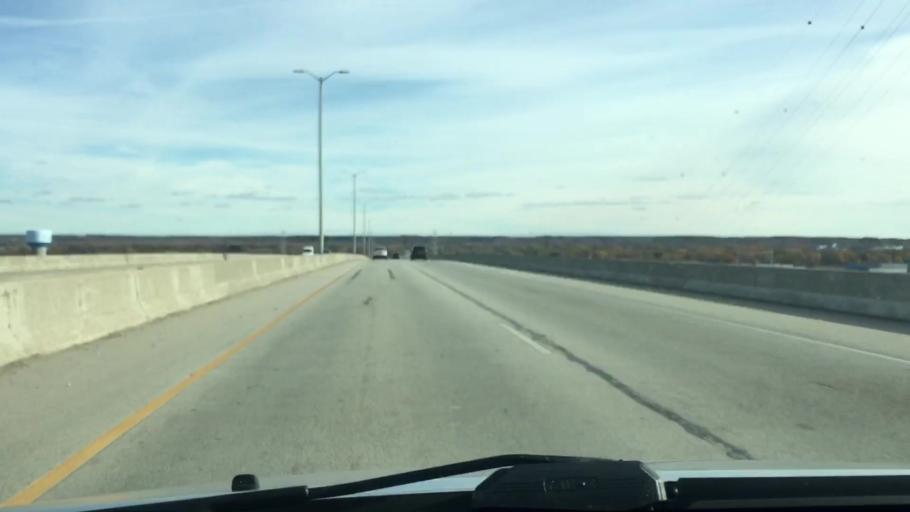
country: US
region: Wisconsin
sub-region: Brown County
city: Green Bay
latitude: 44.5329
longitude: -88.0067
